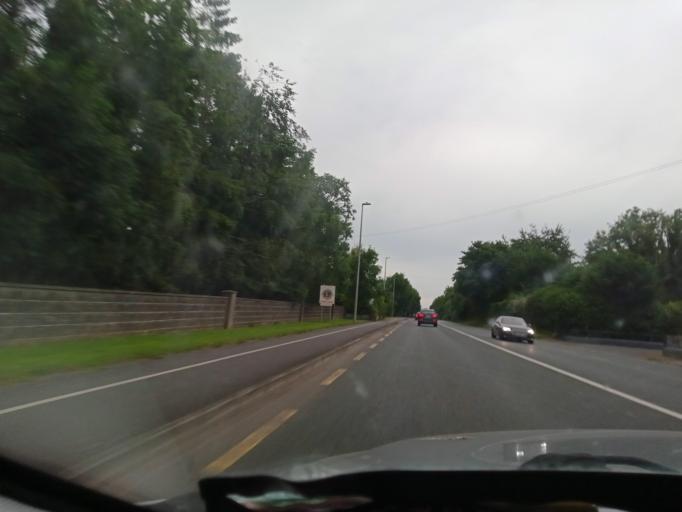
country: IE
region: Leinster
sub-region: Laois
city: Portlaoise
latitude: 53.0175
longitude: -7.3013
